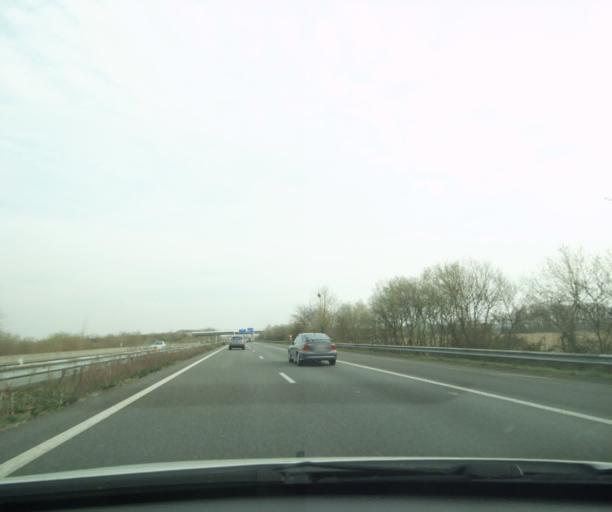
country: FR
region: Aquitaine
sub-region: Departement des Pyrenees-Atlantiques
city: Poey-de-Lescar
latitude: 43.3555
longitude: -0.4517
